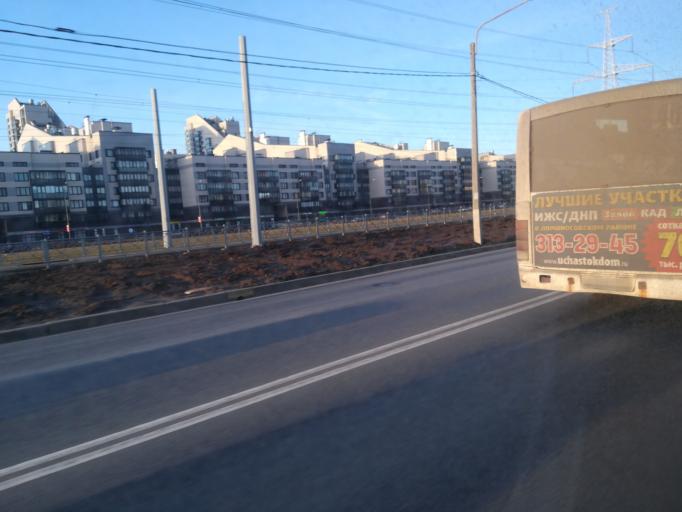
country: RU
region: St.-Petersburg
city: Sosnovaya Polyana
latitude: 59.8468
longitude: 30.1506
